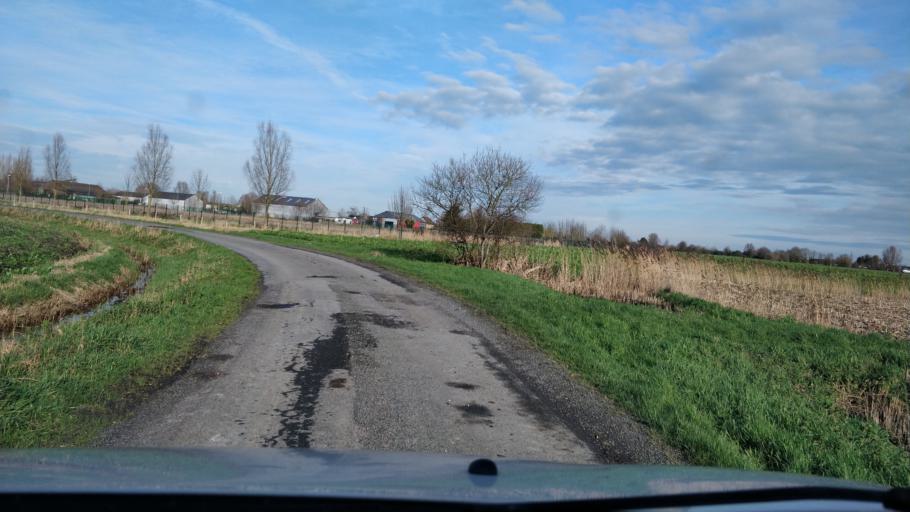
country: FR
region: Brittany
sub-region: Departement d'Ille-et-Vilaine
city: La Fresnais
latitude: 48.5802
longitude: -1.8306
